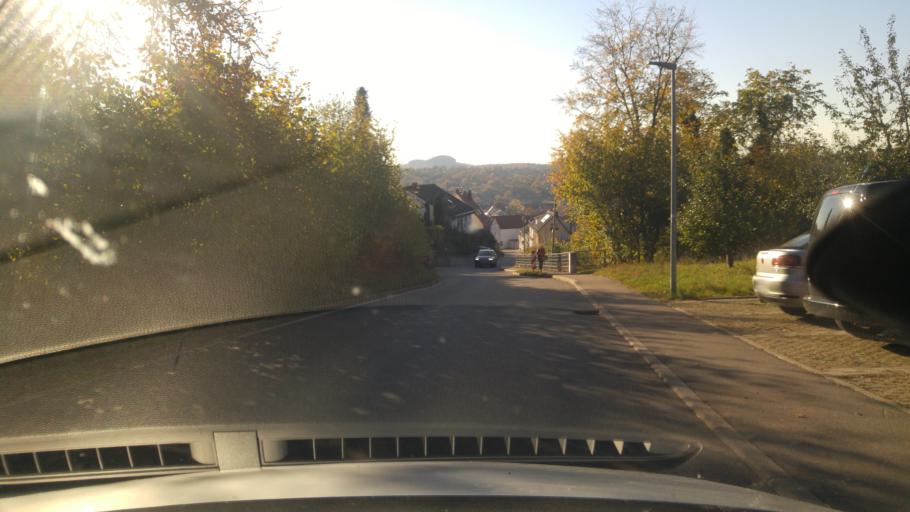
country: DE
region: Baden-Wuerttemberg
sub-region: Regierungsbezirk Stuttgart
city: Owen
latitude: 48.5887
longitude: 9.4562
